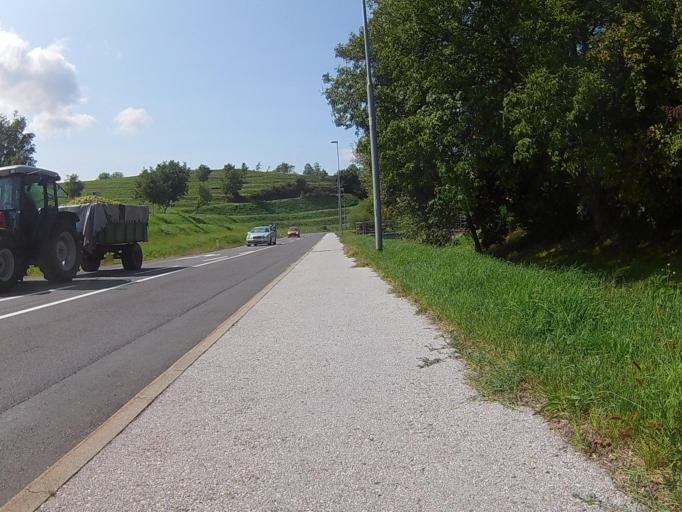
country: SI
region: Ptuj
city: Ptuj
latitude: 46.4260
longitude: 15.8659
